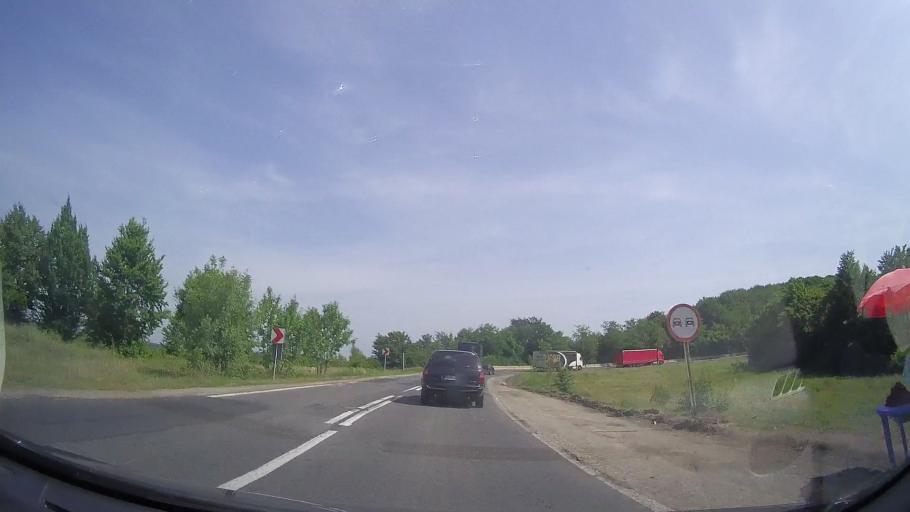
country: RO
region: Timis
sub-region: Comuna Curtea
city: Curtea
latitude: 45.8547
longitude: 22.3260
